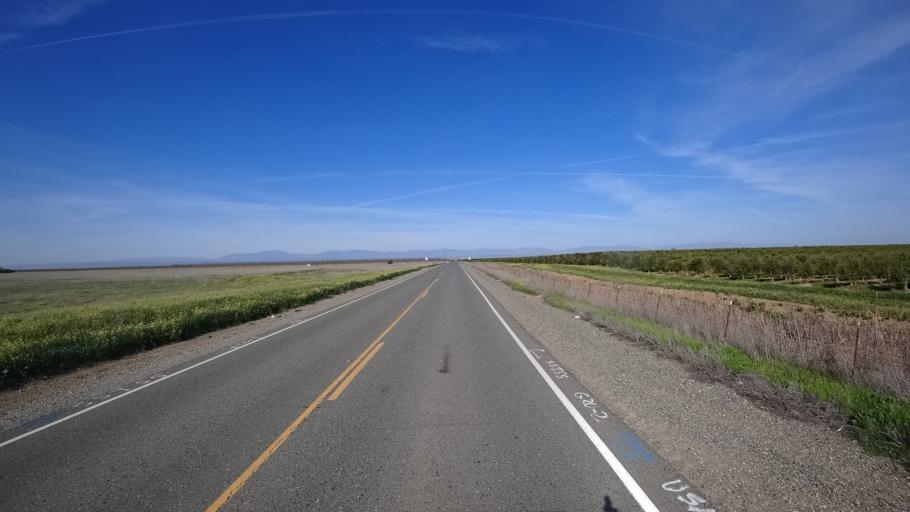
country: US
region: California
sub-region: Glenn County
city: Willows
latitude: 39.6243
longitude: -122.2082
